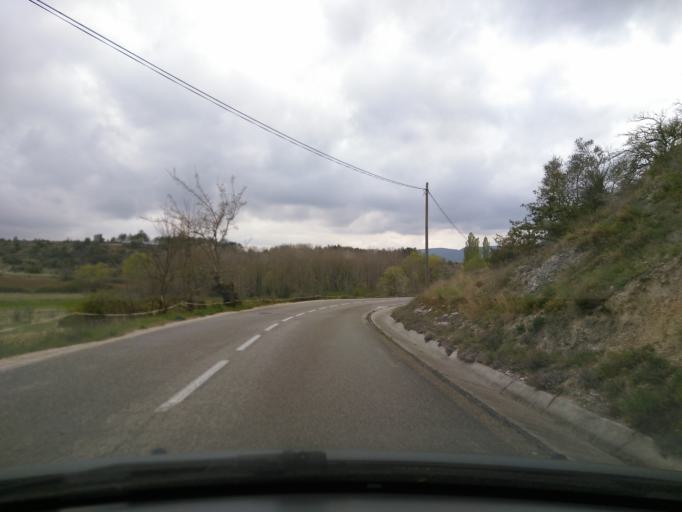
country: FR
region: Languedoc-Roussillon
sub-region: Departement du Gard
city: Barjac
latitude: 44.3520
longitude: 4.3953
